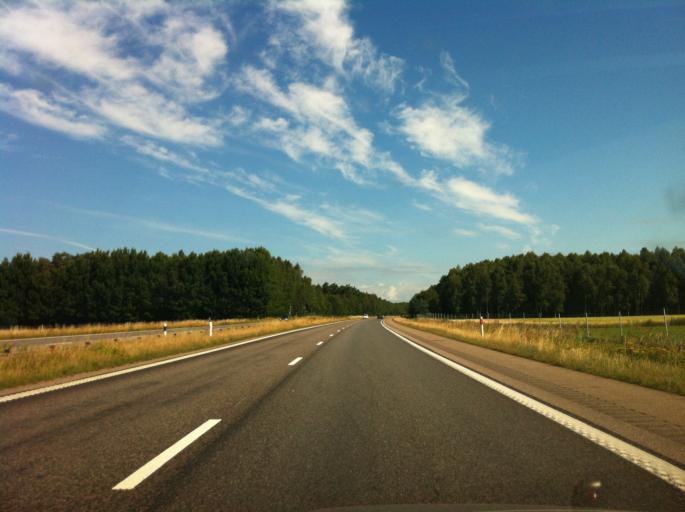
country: SE
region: Halland
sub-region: Laholms Kommun
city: Mellbystrand
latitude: 56.4622
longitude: 12.9422
